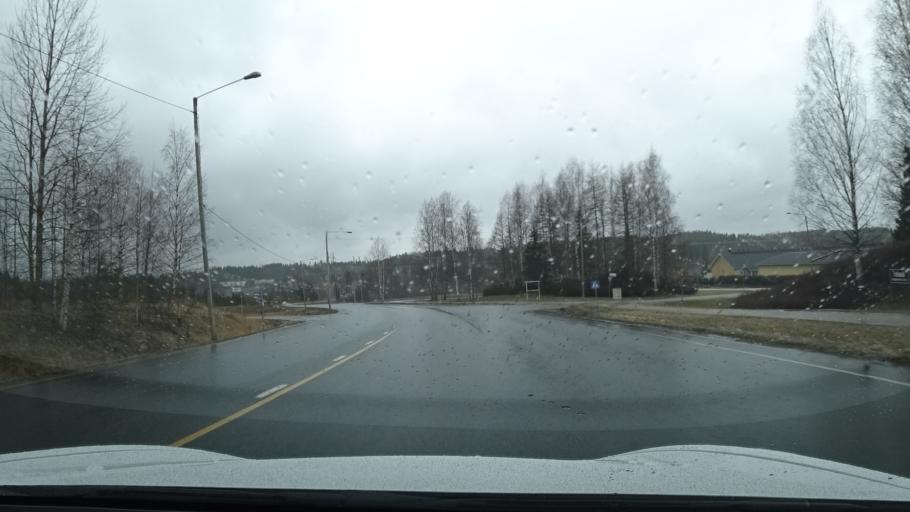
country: FI
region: Paijanne Tavastia
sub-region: Lahti
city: Orimattila
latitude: 60.7956
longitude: 25.7031
